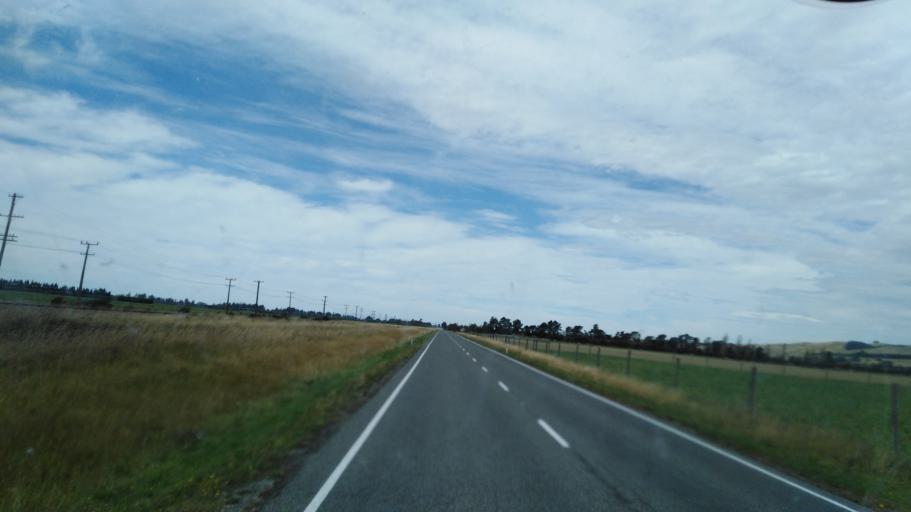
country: NZ
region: Canterbury
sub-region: Selwyn District
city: Darfield
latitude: -43.3612
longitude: 171.9701
